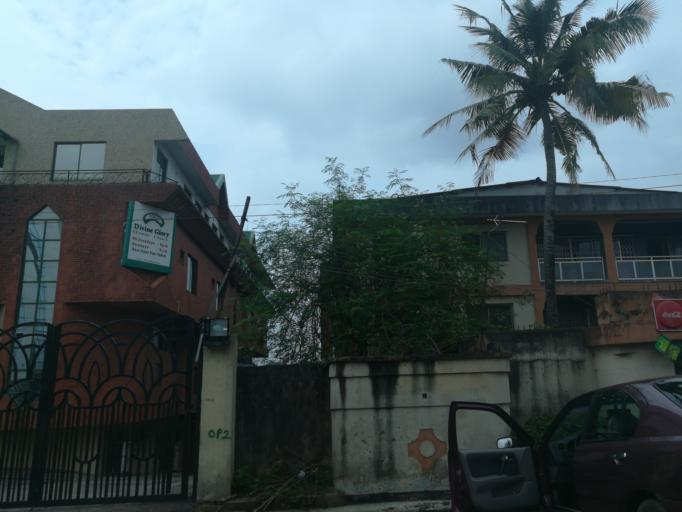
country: NG
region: Lagos
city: Ojota
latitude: 6.5838
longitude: 3.3661
